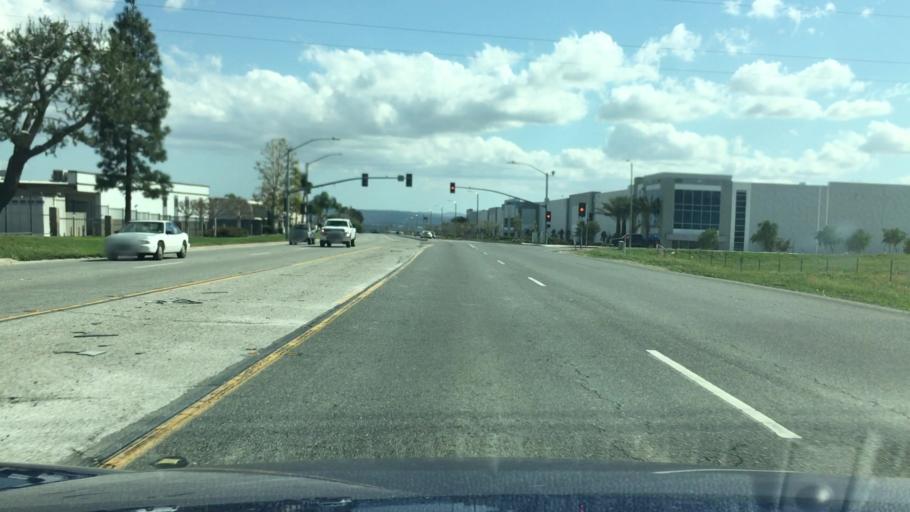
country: US
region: California
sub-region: San Bernardino County
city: Bloomington
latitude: 34.0484
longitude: -117.3701
